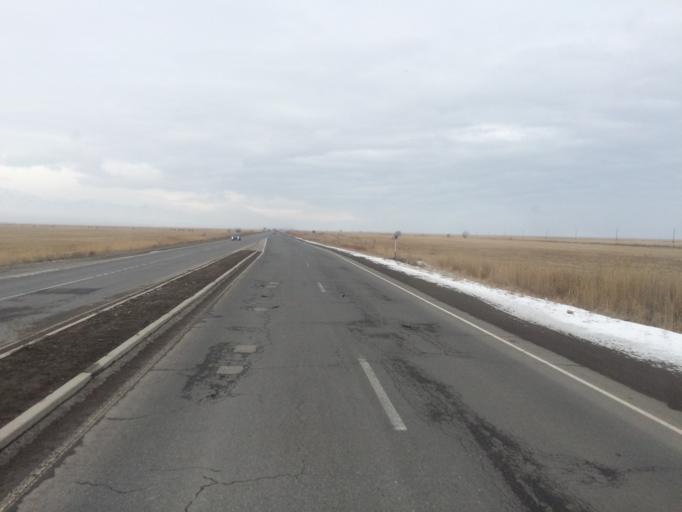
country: KG
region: Chuy
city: Tokmok
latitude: 43.3514
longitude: 75.4669
